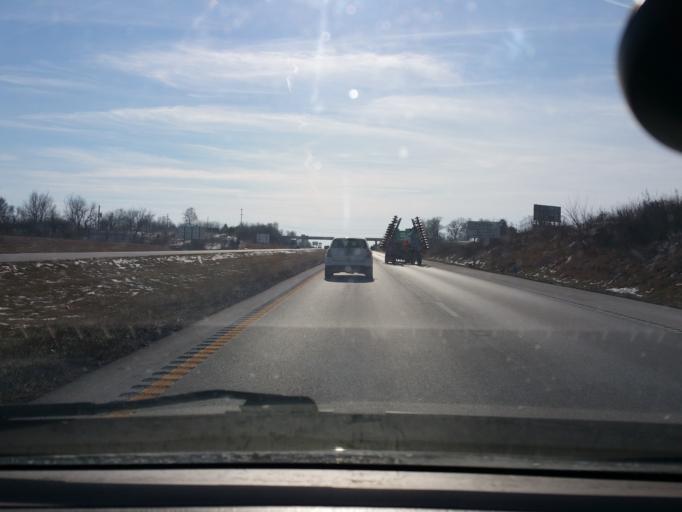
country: US
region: Missouri
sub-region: Clinton County
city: Cameron
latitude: 39.7461
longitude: -94.2202
